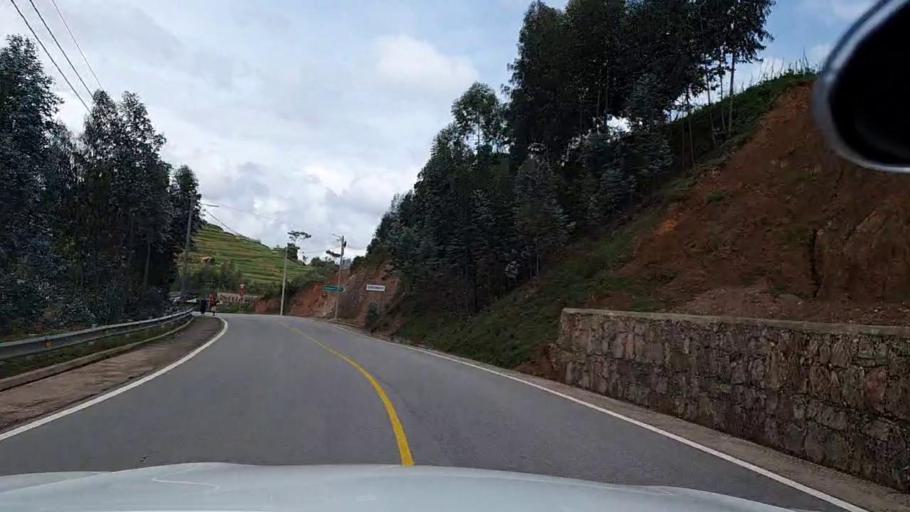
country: RW
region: Southern Province
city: Nzega
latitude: -2.5199
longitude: 29.4581
